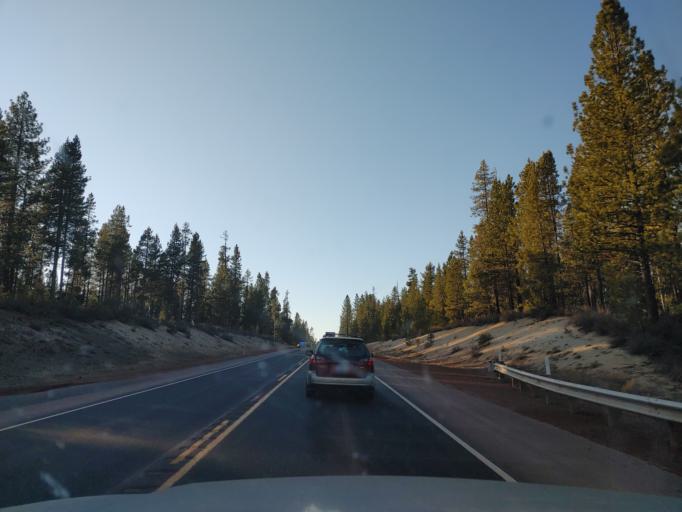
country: US
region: Oregon
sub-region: Deschutes County
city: La Pine
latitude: 43.3808
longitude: -121.8015
